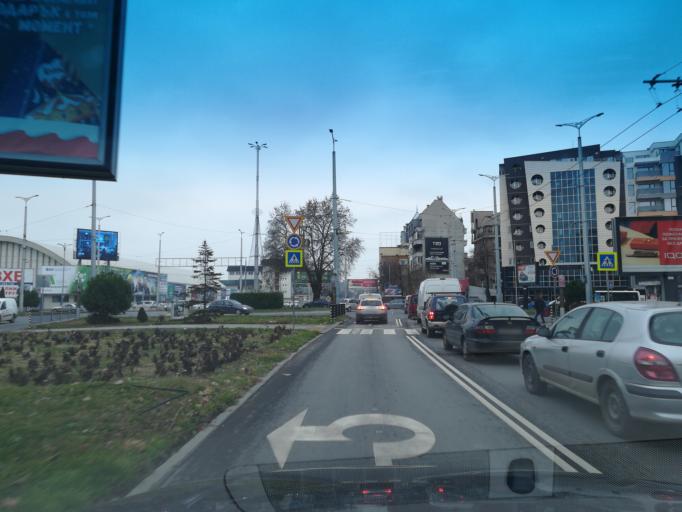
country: BG
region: Plovdiv
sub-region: Obshtina Plovdiv
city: Plovdiv
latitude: 42.1598
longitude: 24.7485
